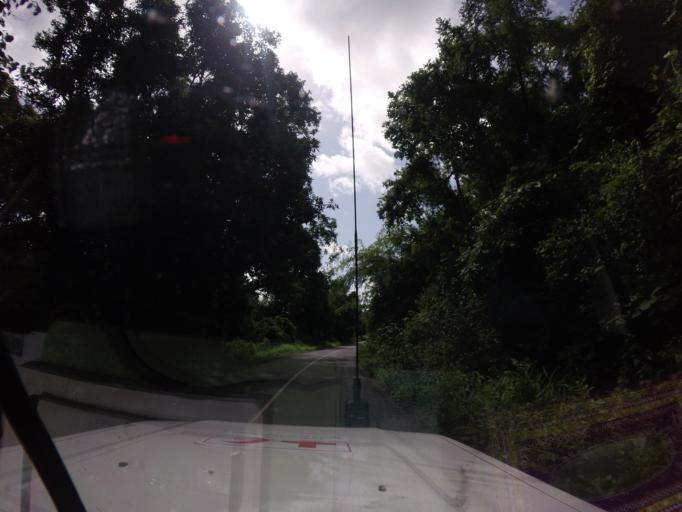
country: GN
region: Mamou
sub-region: Mamou Prefecture
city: Mamou
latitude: 10.2443
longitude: -11.8807
